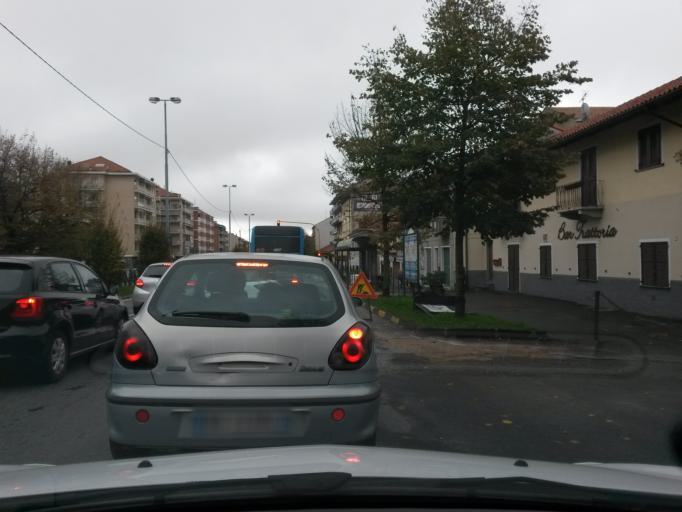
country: IT
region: Piedmont
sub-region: Provincia di Torino
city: Rivoli
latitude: 45.0710
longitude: 7.5385
